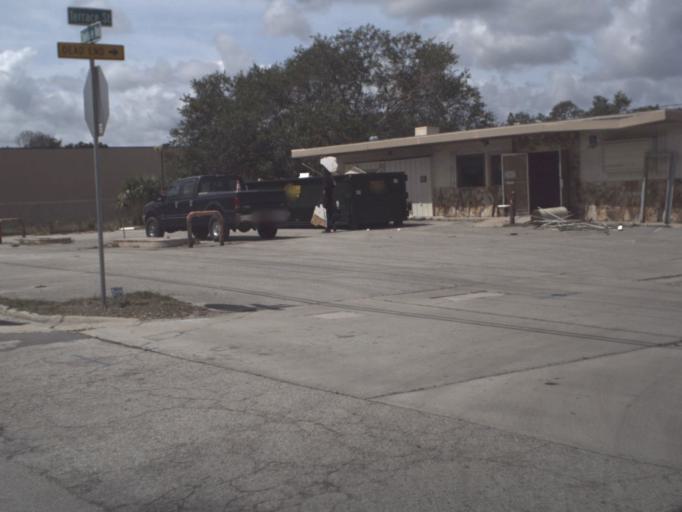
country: US
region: Florida
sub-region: Brevard County
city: Cocoa West
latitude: 28.3637
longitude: -80.7551
